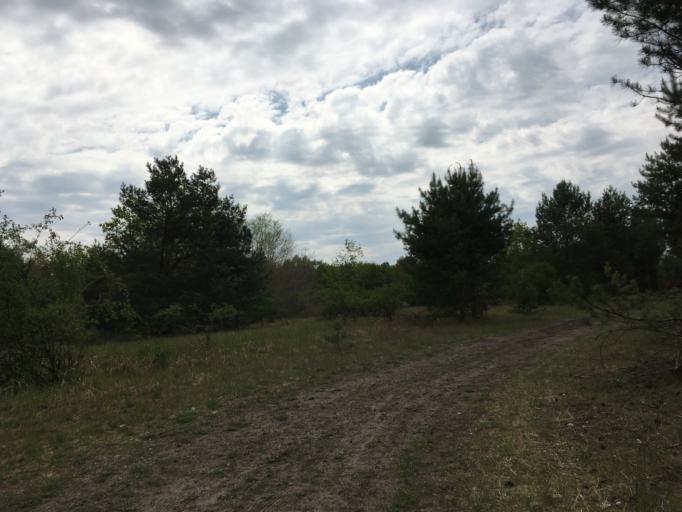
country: DE
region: Brandenburg
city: Rudnitz
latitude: 52.6985
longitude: 13.6154
